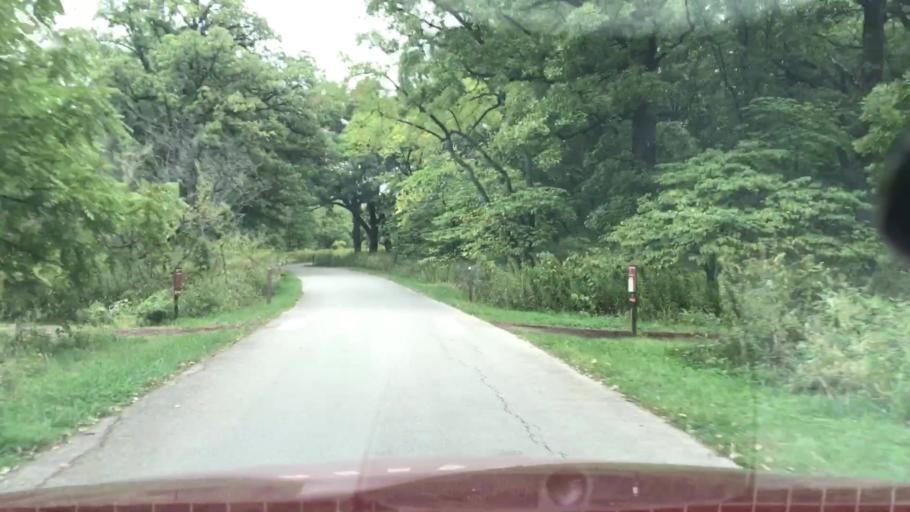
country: US
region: Illinois
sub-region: DuPage County
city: Lisle
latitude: 41.8155
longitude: -88.0584
